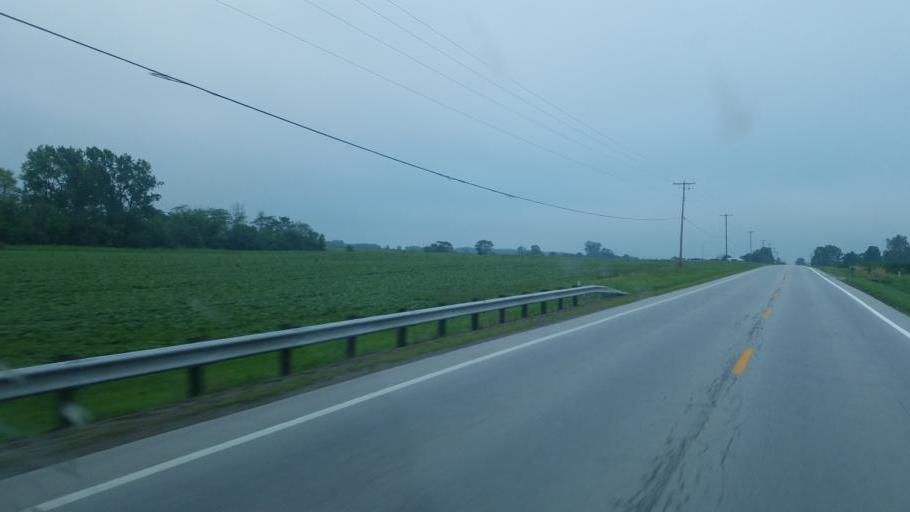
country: US
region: Ohio
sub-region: Fayette County
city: Washington Court House
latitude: 39.6113
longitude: -83.3680
